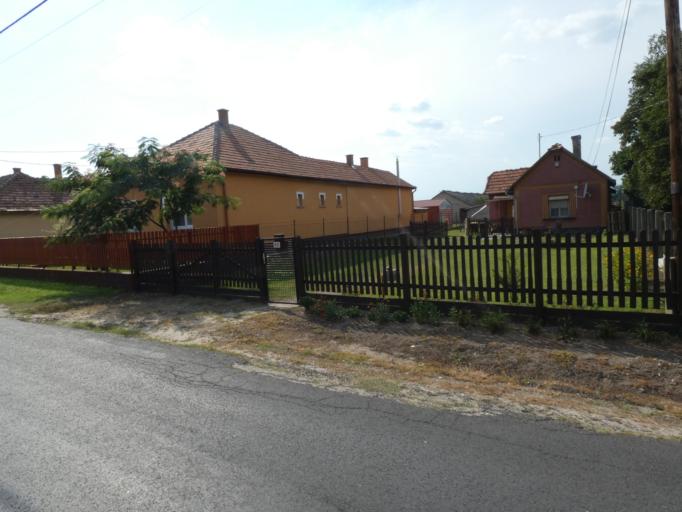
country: HU
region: Pest
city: Taborfalva
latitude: 47.1072
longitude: 19.4875
